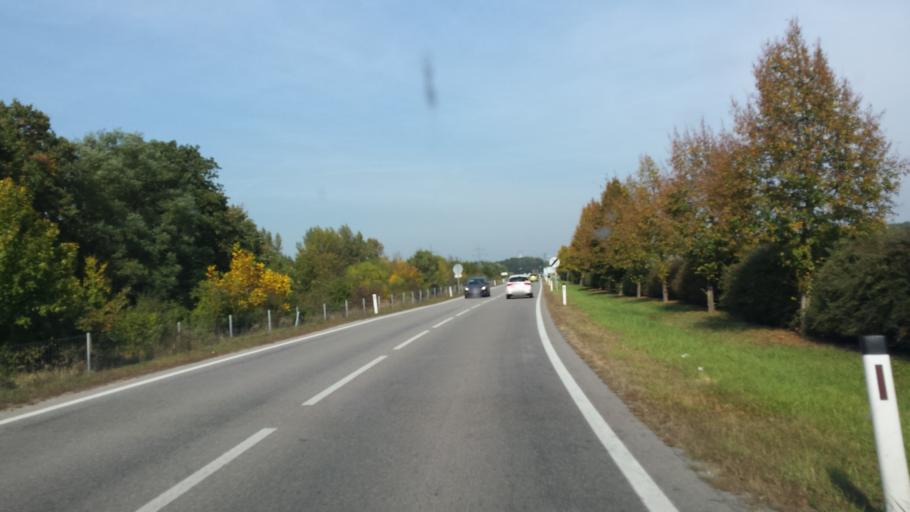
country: AT
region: Lower Austria
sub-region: Politischer Bezirk Tulln
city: Langenrohr
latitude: 48.3177
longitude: 16.0305
